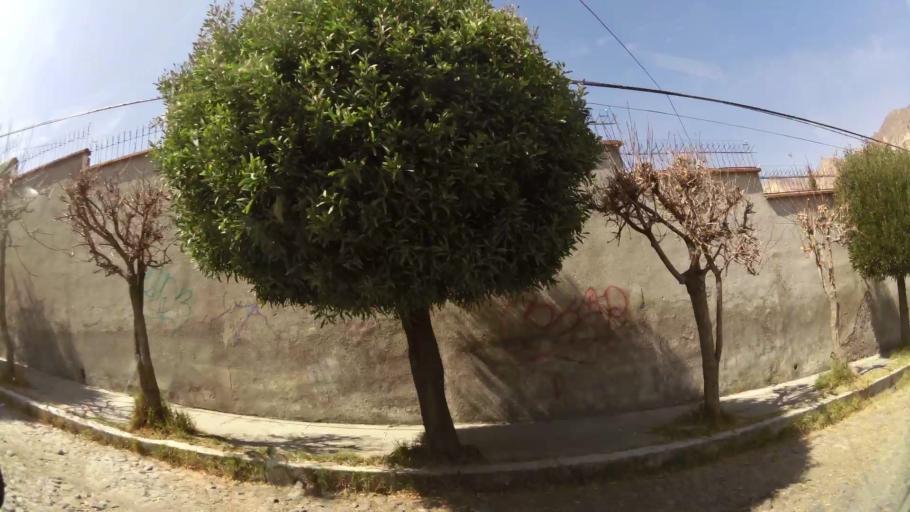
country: BO
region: La Paz
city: La Paz
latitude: -16.5429
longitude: -68.0596
